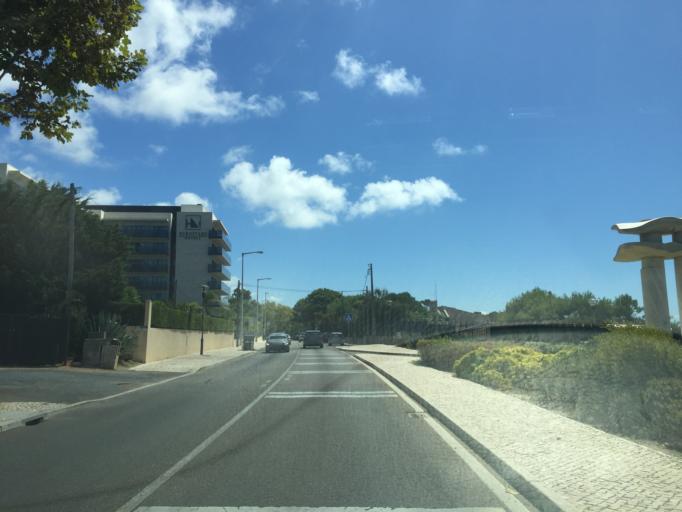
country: PT
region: Lisbon
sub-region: Cascais
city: Cascais
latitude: 38.6955
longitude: -9.4375
